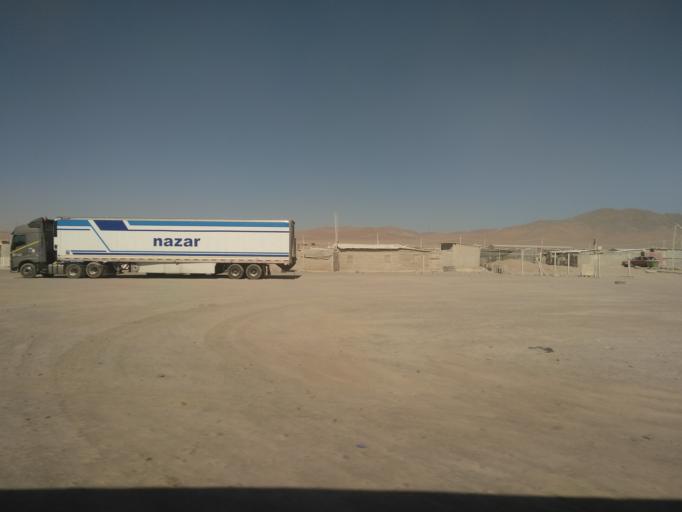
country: CL
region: Antofagasta
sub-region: Provincia de Antofagasta
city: Antofagasta
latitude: -23.7869
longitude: -70.3168
